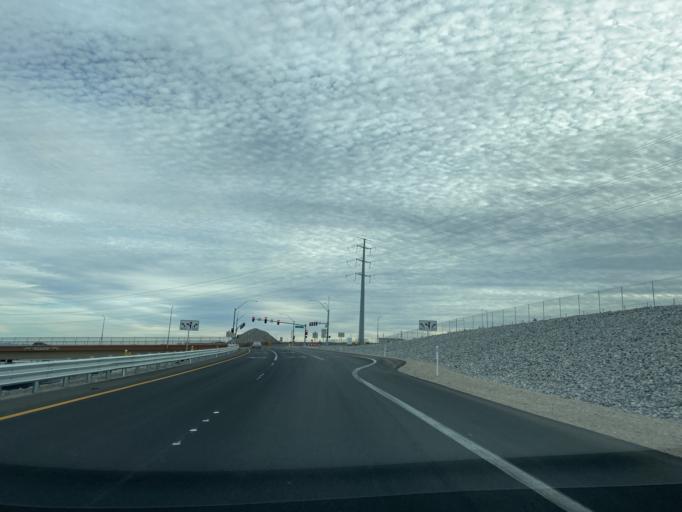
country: US
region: Nevada
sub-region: Clark County
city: Summerlin South
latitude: 36.2627
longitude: -115.3281
